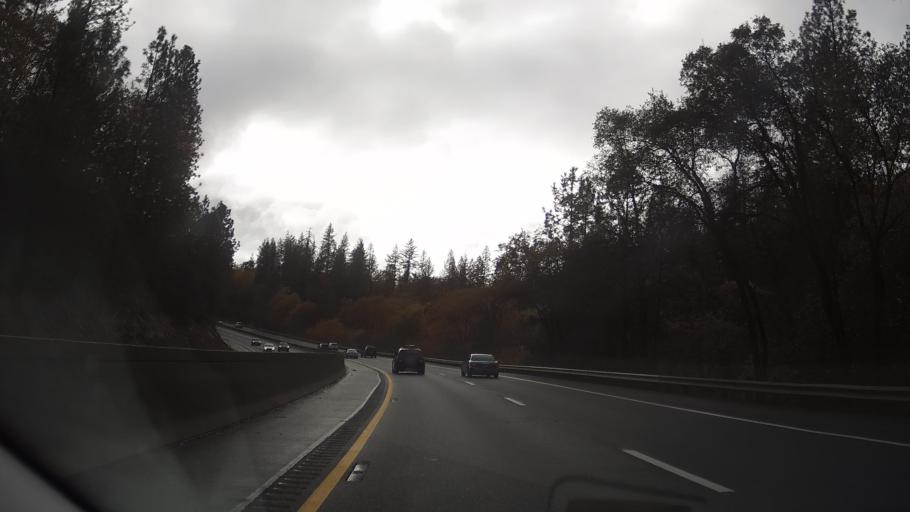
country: US
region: California
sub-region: Placer County
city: Meadow Vista
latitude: 39.0150
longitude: -120.9890
